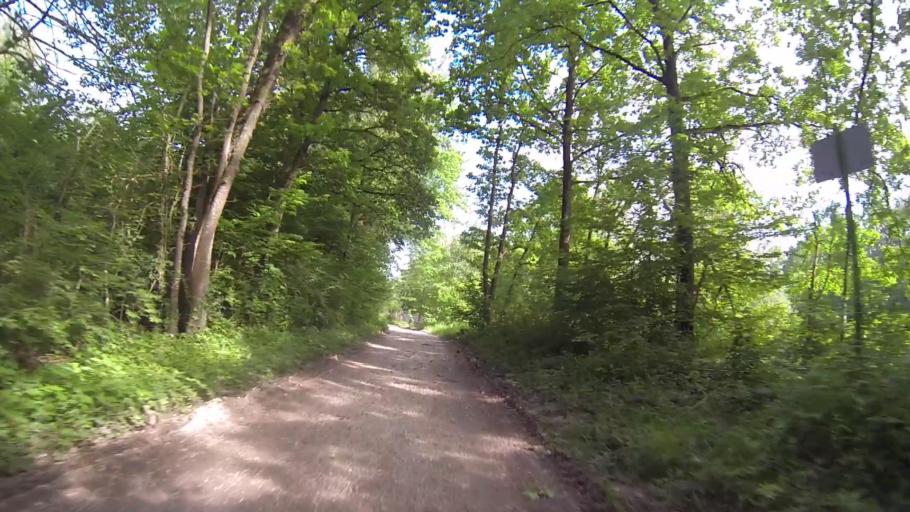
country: DE
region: Bavaria
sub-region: Swabia
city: Senden
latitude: 48.3310
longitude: 10.0180
